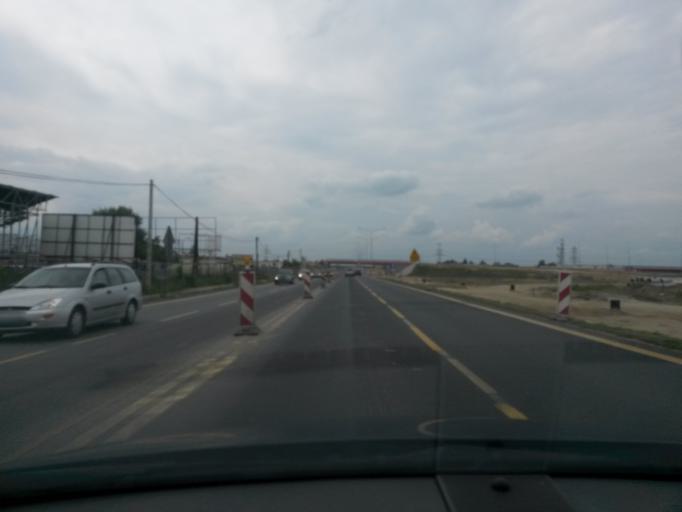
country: PL
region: Masovian Voivodeship
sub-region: Powiat pruszkowski
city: Nowe Grocholice
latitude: 52.1271
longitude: 20.8816
